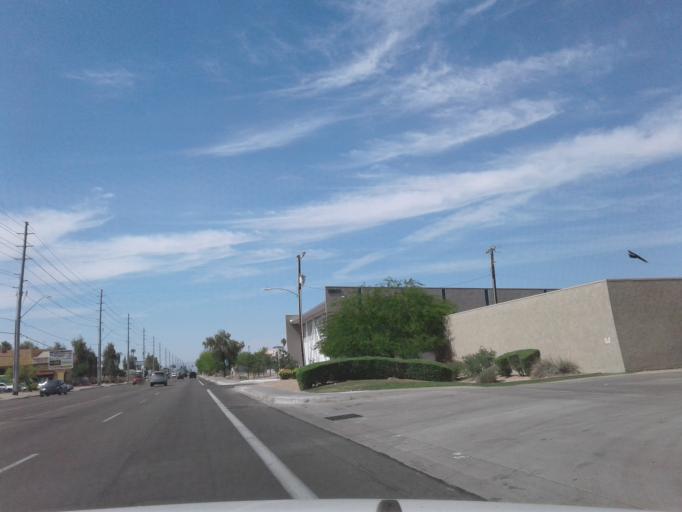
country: US
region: Arizona
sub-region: Maricopa County
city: Paradise Valley
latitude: 33.6294
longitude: -112.0133
